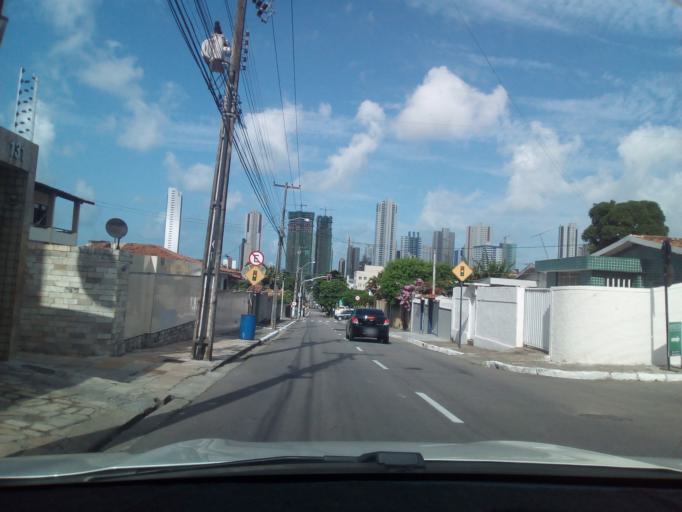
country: BR
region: Paraiba
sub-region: Joao Pessoa
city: Joao Pessoa
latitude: -7.1145
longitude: -34.8484
